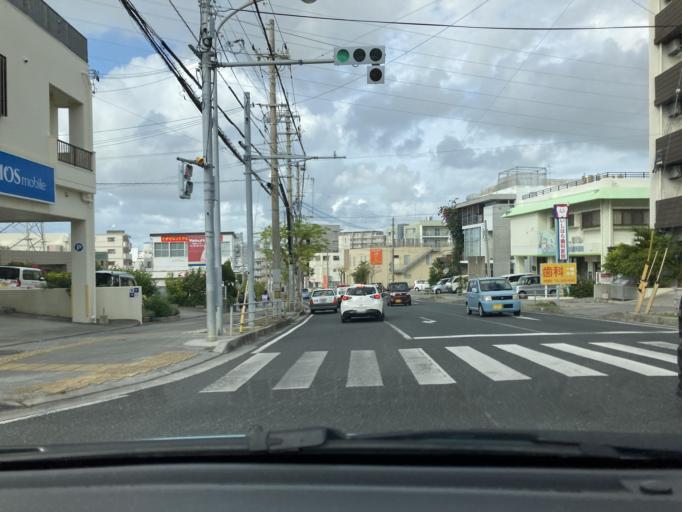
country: JP
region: Okinawa
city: Tomigusuku
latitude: 26.1901
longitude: 127.6745
